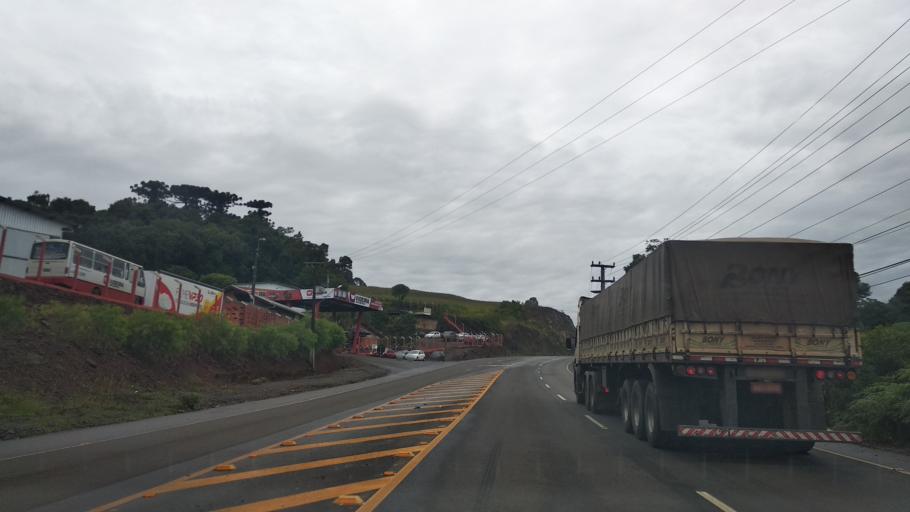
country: BR
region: Santa Catarina
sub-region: Videira
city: Videira
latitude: -27.0376
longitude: -51.1543
